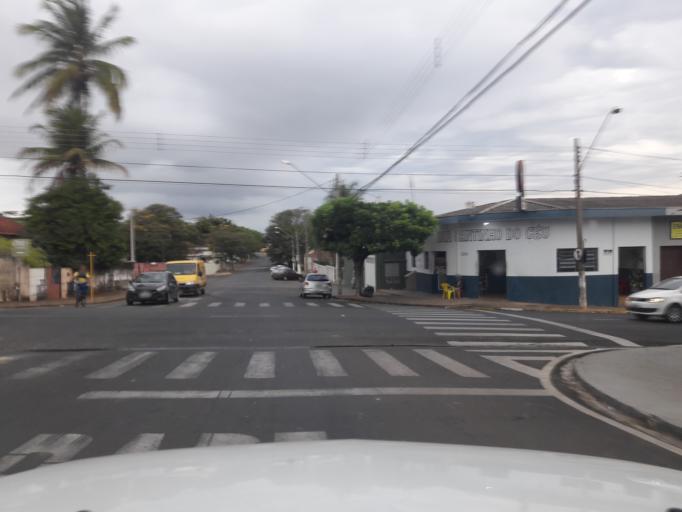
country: BR
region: Sao Paulo
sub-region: Moji-Guacu
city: Mogi-Gaucu
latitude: -22.3642
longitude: -46.9488
